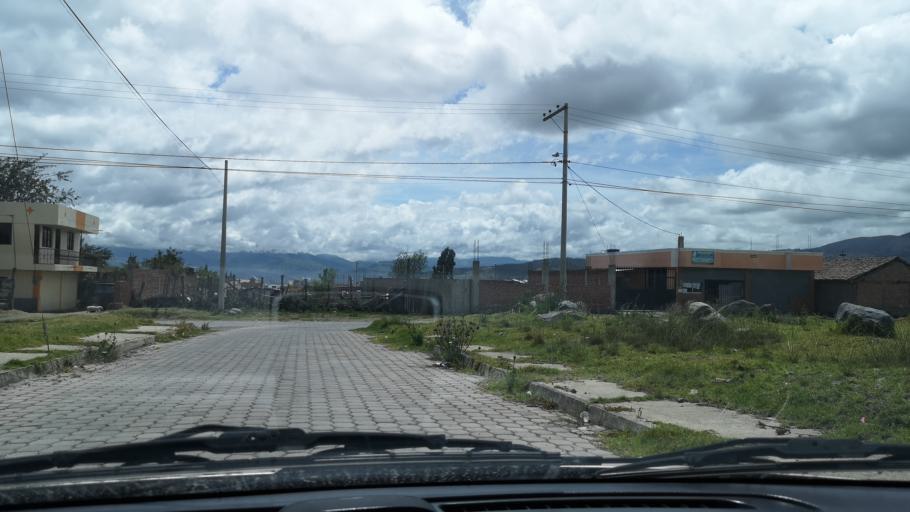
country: EC
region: Chimborazo
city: Riobamba
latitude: -1.6415
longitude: -78.6838
